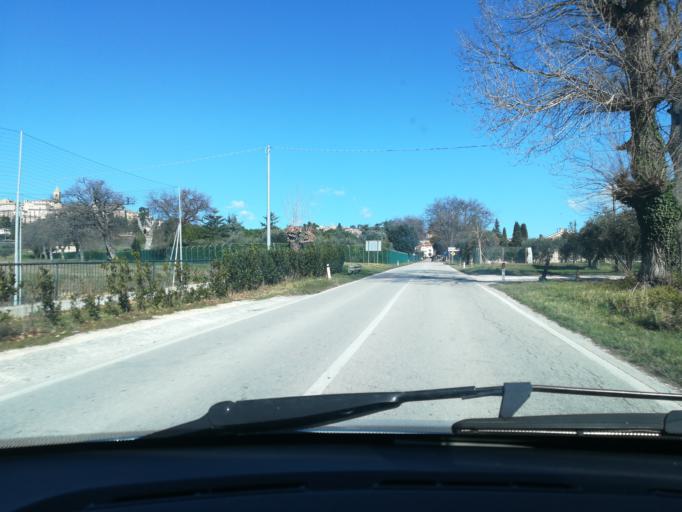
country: IT
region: The Marches
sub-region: Provincia di Macerata
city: Montecassiano
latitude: 43.3581
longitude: 13.4406
